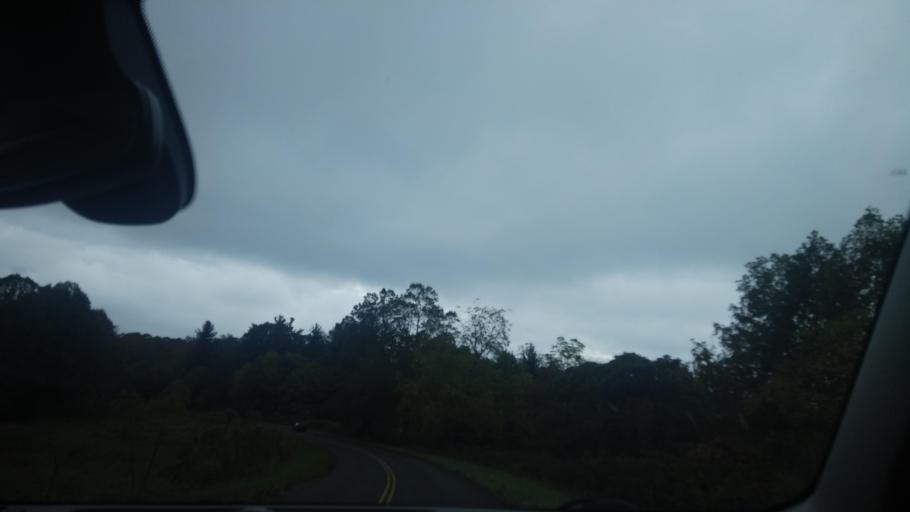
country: US
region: Virginia
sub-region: Carroll County
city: Cana
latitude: 36.6704
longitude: -80.6336
